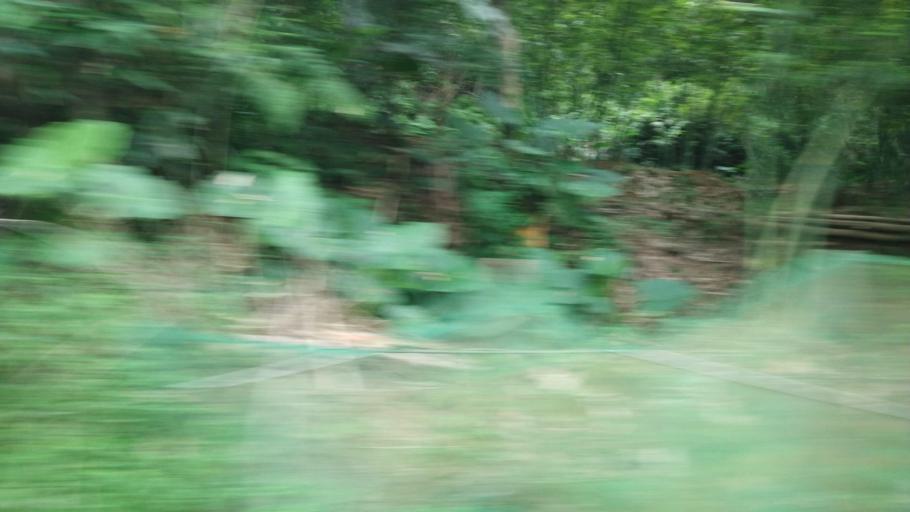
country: TW
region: Taiwan
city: Daxi
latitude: 24.9116
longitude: 121.3909
